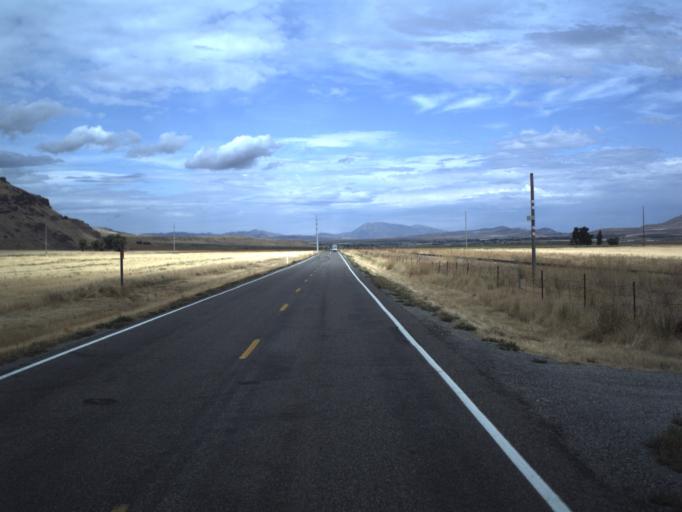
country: US
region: Utah
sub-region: Cache County
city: Benson
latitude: 41.7790
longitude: -111.9849
